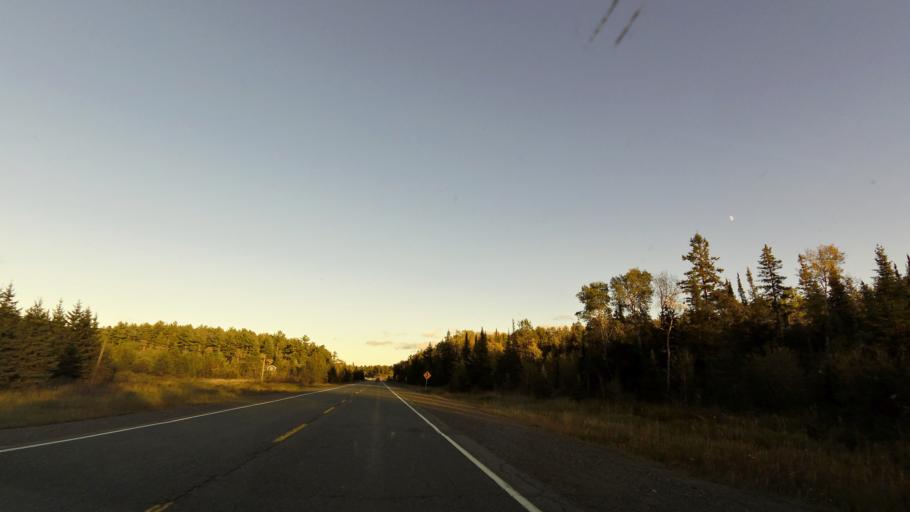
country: CA
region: Ontario
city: Espanola
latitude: 46.3329
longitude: -81.5125
